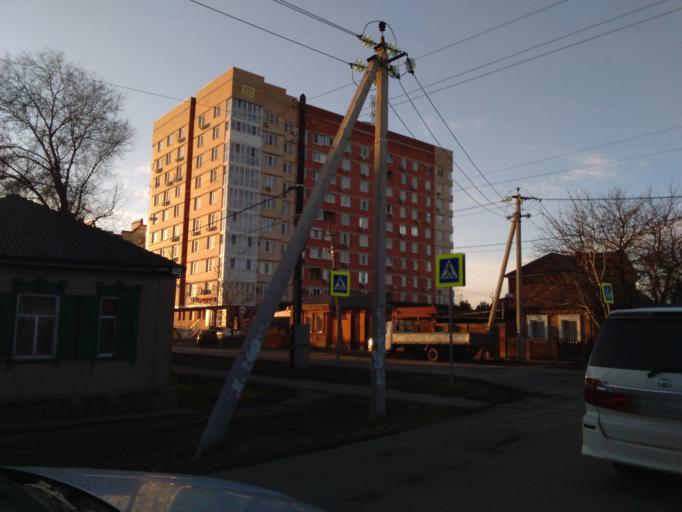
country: RU
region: Rostov
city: Bataysk
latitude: 47.1429
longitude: 39.7439
